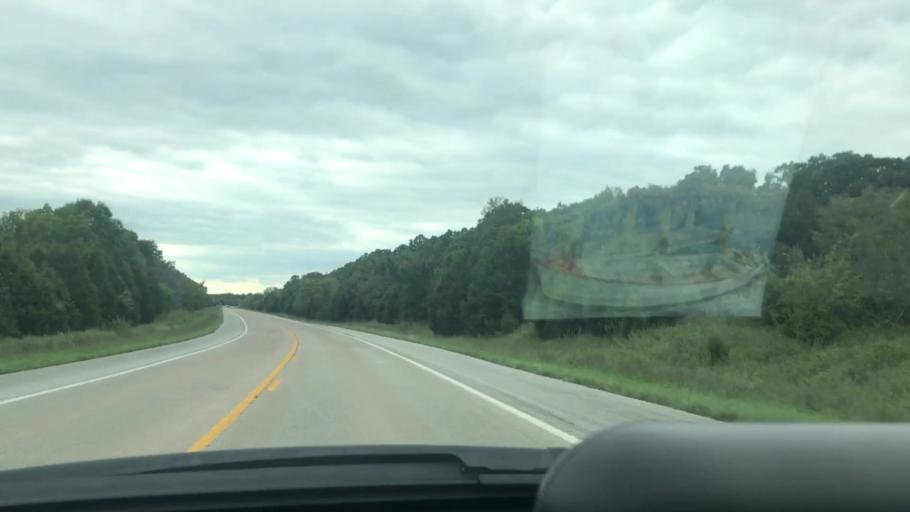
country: US
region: Missouri
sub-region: Benton County
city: Warsaw
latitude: 38.2085
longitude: -93.3313
